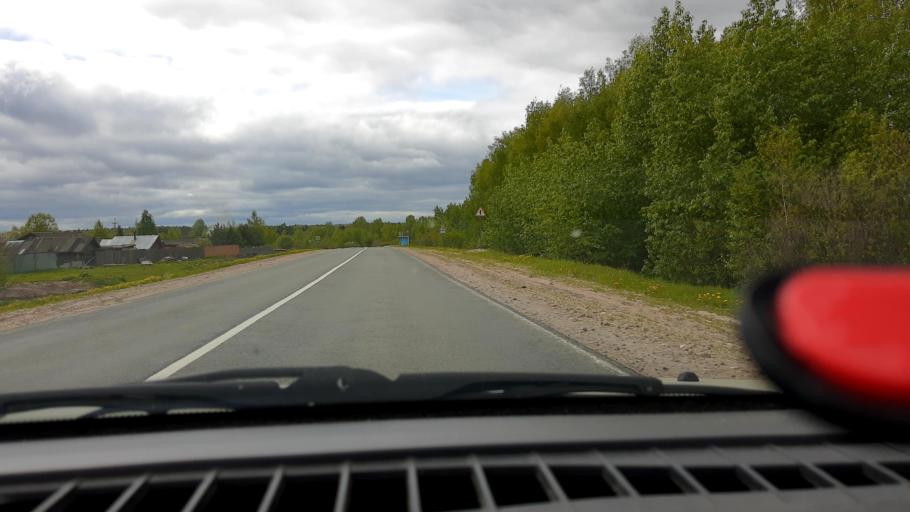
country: RU
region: Nizjnij Novgorod
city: Uren'
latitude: 57.2418
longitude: 45.5723
